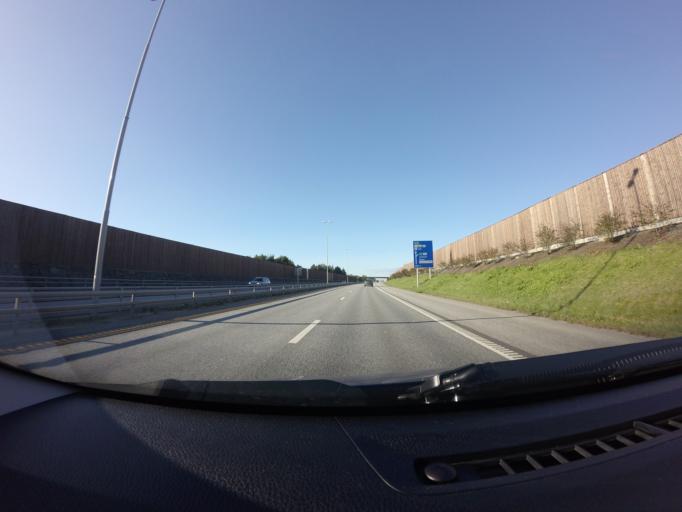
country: NO
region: Rogaland
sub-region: Sandnes
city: Sandnes
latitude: 58.8506
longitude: 5.7144
